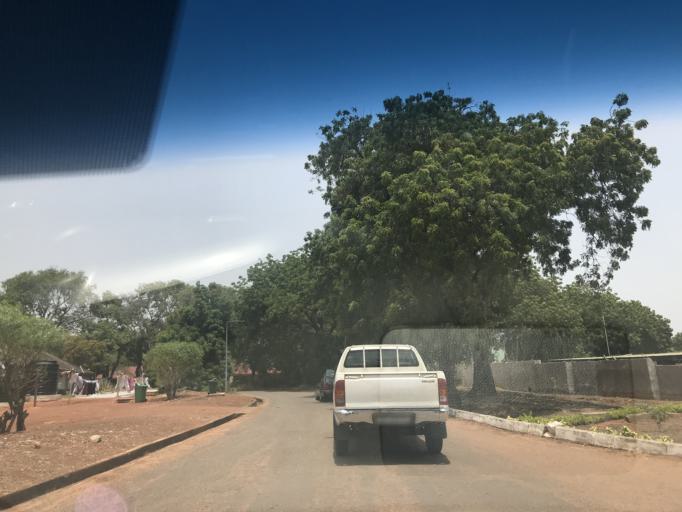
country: GH
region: Greater Accra
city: Teshi Old Town
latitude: 5.5855
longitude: -0.1538
